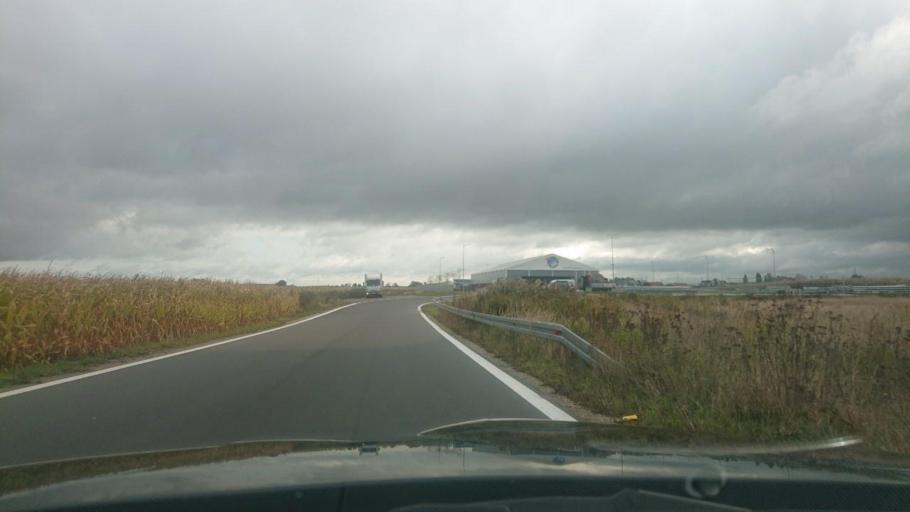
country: PL
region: Greater Poland Voivodeship
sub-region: Powiat gnieznienski
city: Gniezno
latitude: 52.5254
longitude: 17.6324
